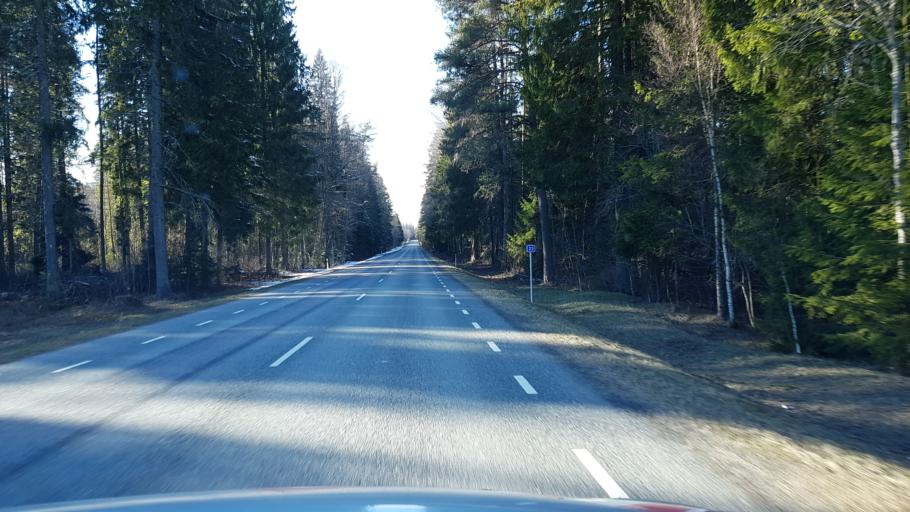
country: EE
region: Laeaene-Virumaa
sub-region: Tapa vald
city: Tapa
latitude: 59.4298
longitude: 25.9750
